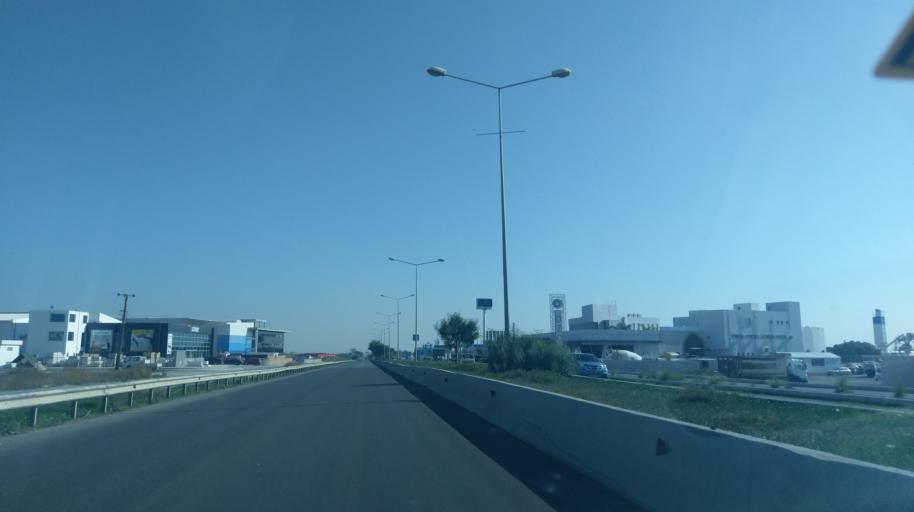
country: CY
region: Lefkosia
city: Nicosia
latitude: 35.2162
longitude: 33.4260
